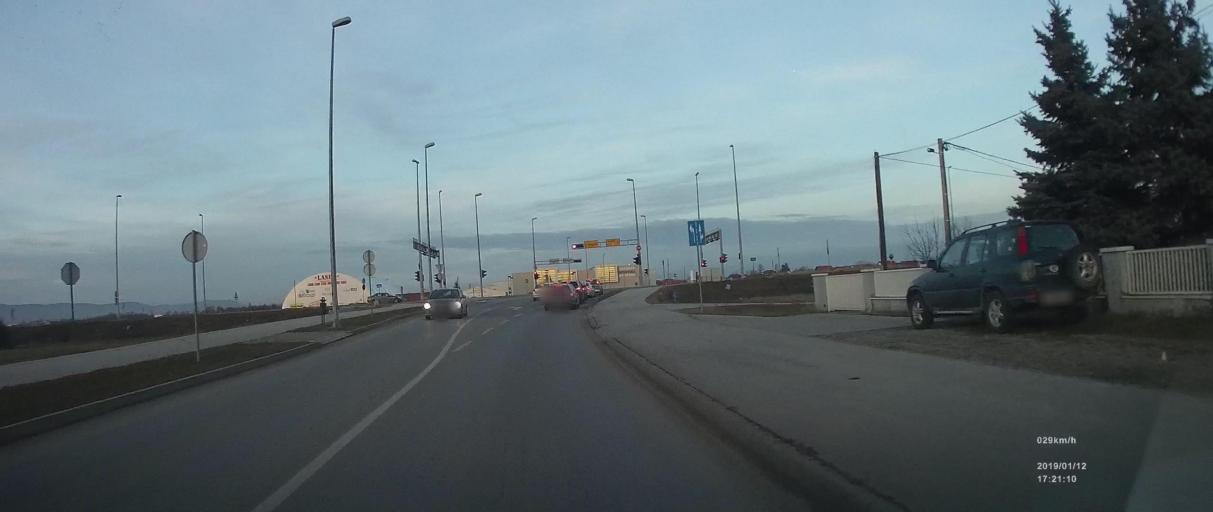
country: HR
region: Zagrebacka
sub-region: Grad Velika Gorica
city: Velika Gorica
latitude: 45.7195
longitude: 16.0782
